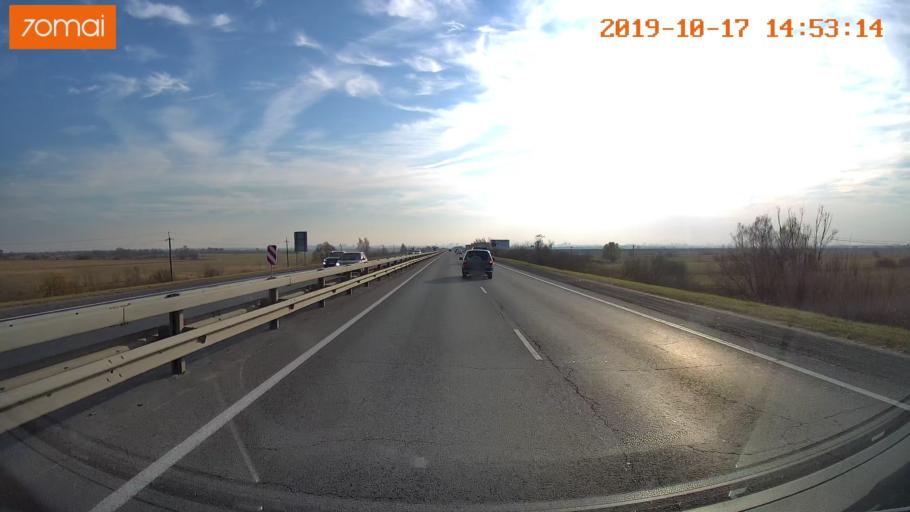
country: RU
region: Rjazan
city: Polyany
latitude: 54.6965
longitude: 39.8400
